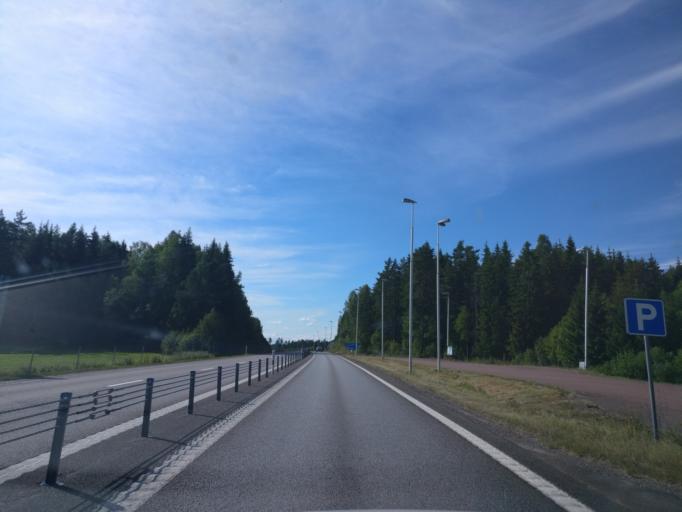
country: SE
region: Vaermland
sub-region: Kils Kommun
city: Kil
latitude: 59.4872
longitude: 13.3430
